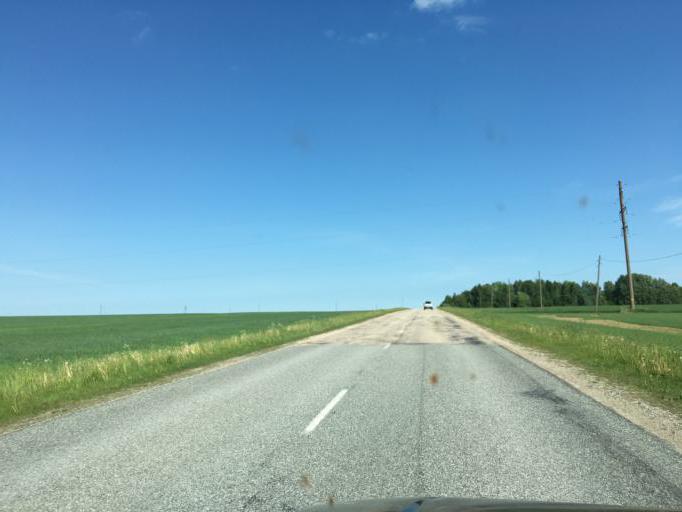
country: LV
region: Talsu Rajons
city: Valdemarpils
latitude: 57.3585
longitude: 22.4928
